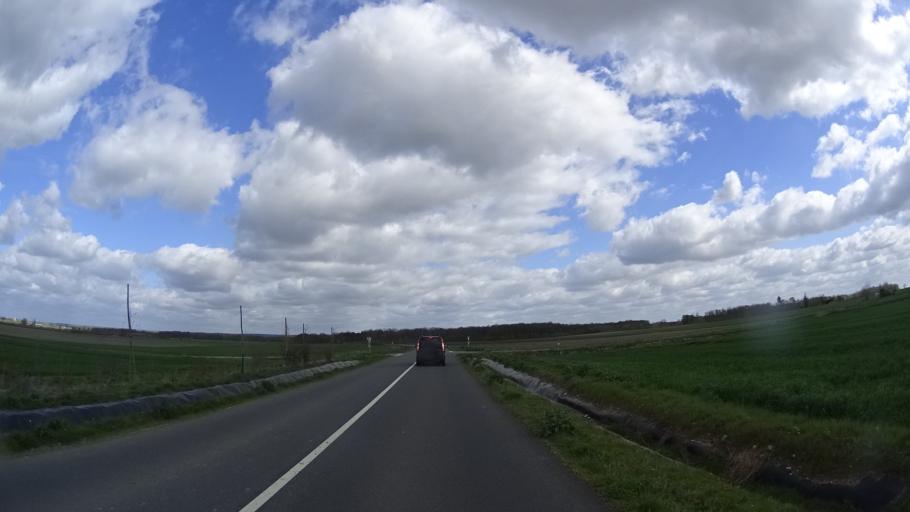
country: FR
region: Pays de la Loire
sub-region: Departement de Maine-et-Loire
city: Breze
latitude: 47.0806
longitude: -0.0159
